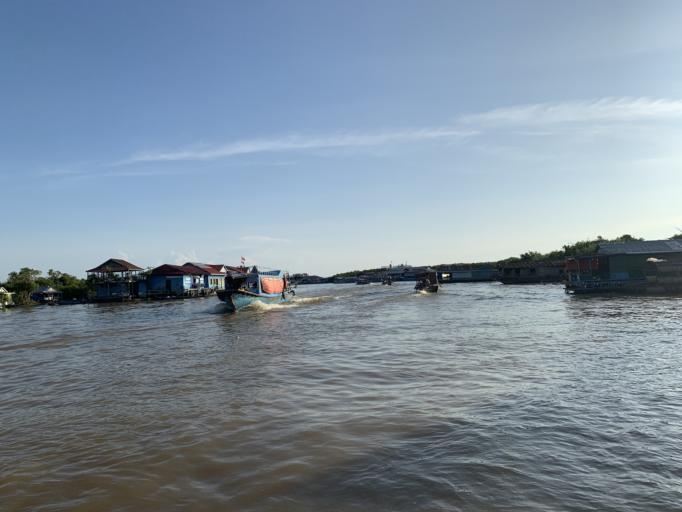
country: KH
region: Siem Reap
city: Siem Reap
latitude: 13.2454
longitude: 103.8231
